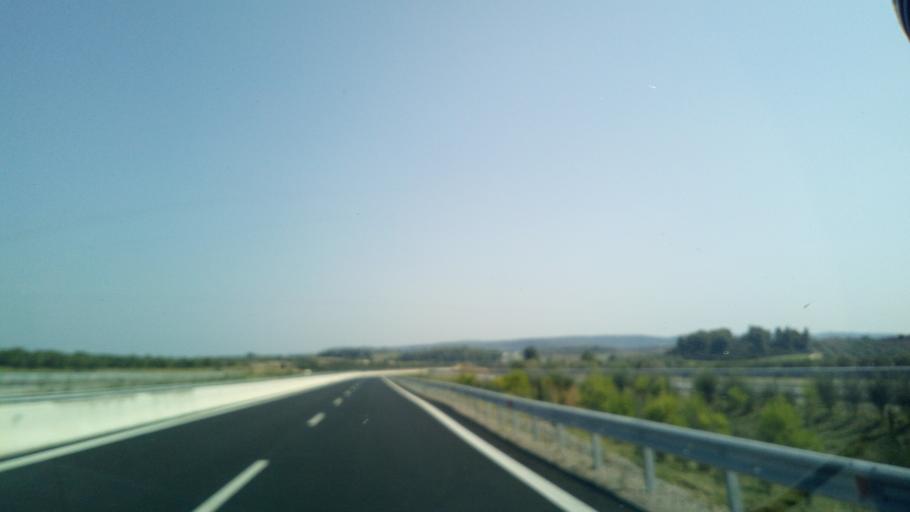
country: GR
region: Central Macedonia
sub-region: Nomos Chalkidikis
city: Afytos
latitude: 40.0856
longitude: 23.4147
